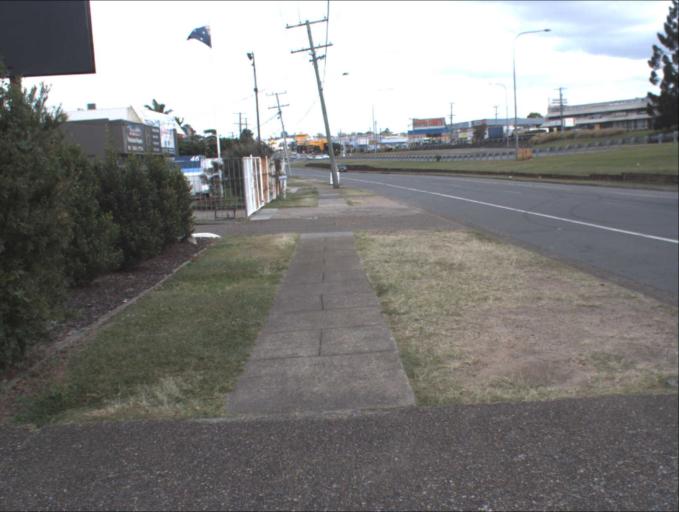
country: AU
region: Queensland
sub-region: Logan
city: Springwood
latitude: -27.6127
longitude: 153.1175
